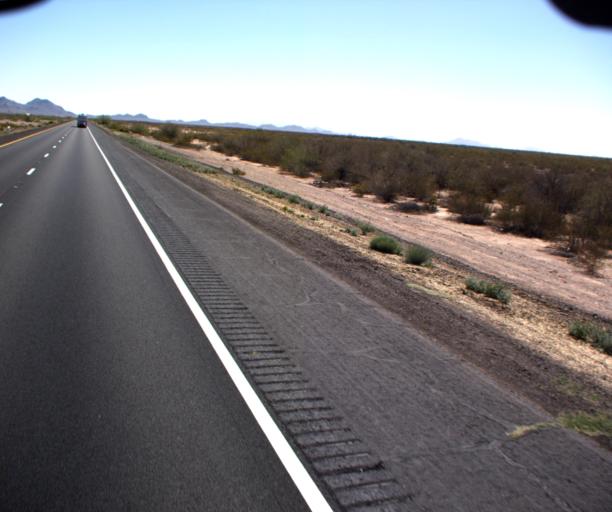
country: US
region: Arizona
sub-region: La Paz County
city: Salome
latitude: 33.6262
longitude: -113.7374
